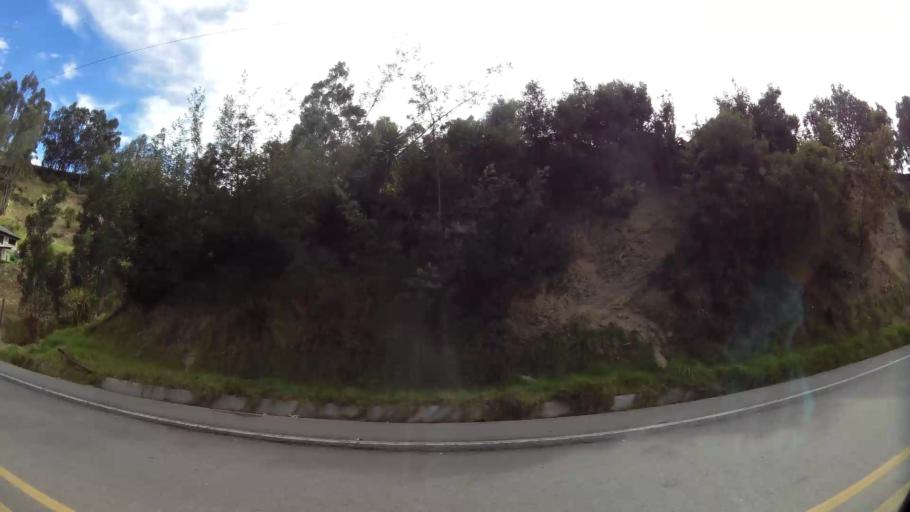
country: EC
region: Canar
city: Azogues
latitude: -2.7287
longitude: -78.8615
